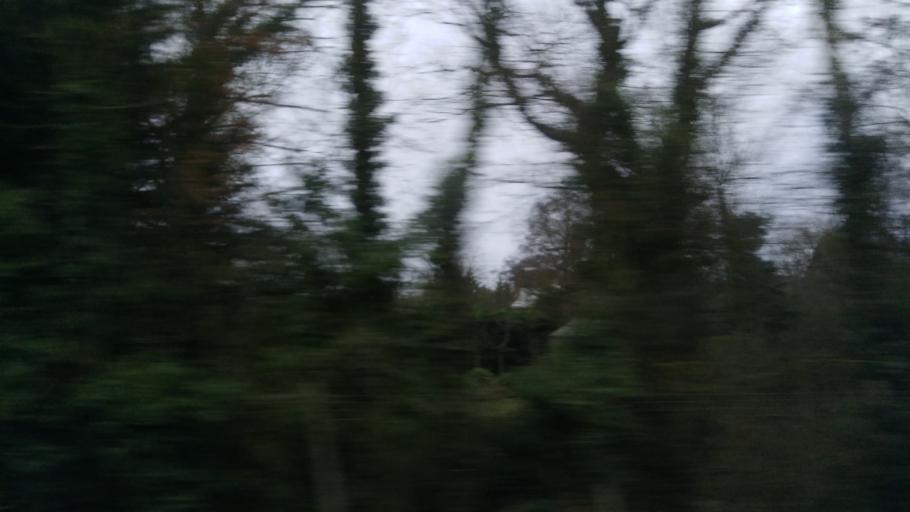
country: GB
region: England
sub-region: Kent
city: Marden
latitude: 51.1781
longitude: 0.4529
